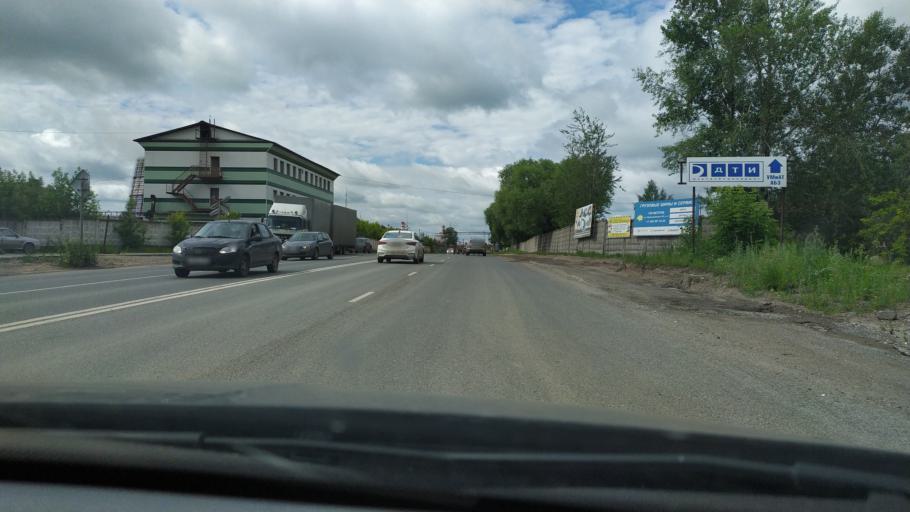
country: RU
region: Perm
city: Kondratovo
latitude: 57.9305
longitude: 56.1462
